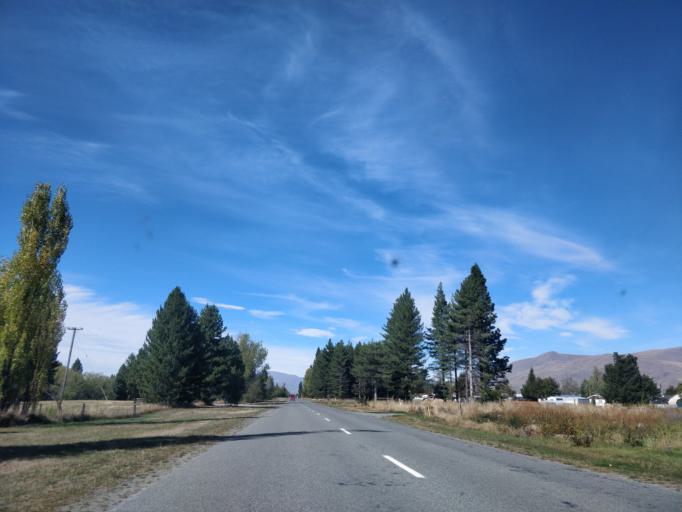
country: NZ
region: Canterbury
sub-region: Timaru District
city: Pleasant Point
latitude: -44.2490
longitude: 170.0974
